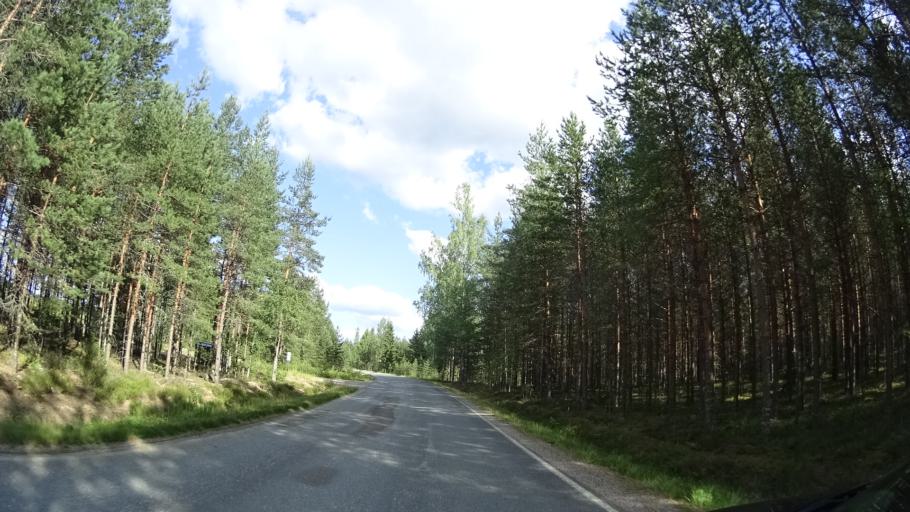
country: FI
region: Uusimaa
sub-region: Helsinki
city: Kaerkoelae
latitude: 60.7398
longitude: 24.0907
